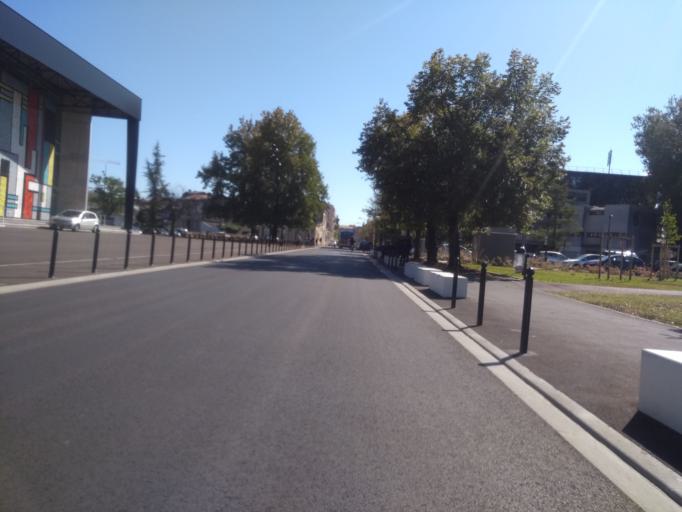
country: FR
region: Aquitaine
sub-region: Departement de la Gironde
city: Bordeaux
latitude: 44.8571
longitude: -0.5795
